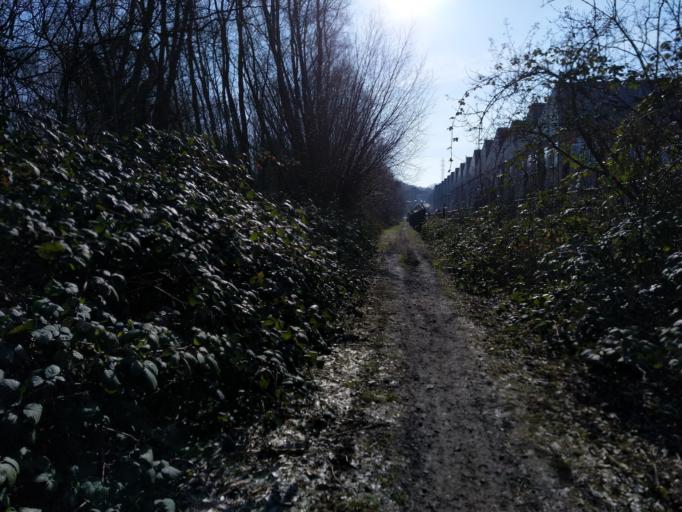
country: BE
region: Wallonia
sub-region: Province du Hainaut
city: Mons
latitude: 50.4440
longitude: 3.9375
